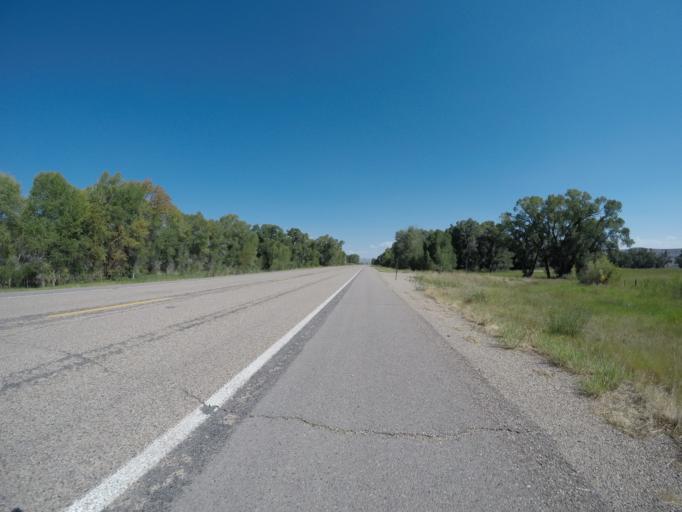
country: US
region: Wyoming
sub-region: Sublette County
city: Marbleton
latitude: 42.2202
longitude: -110.1906
